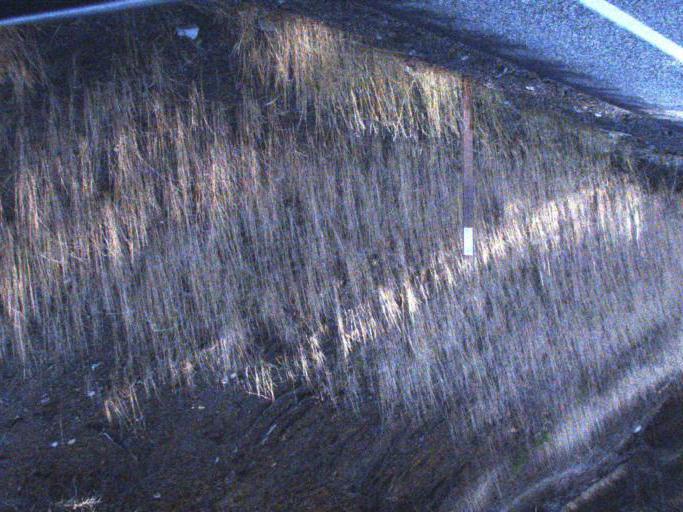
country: US
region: Washington
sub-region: Ferry County
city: Republic
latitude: 48.6110
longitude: -118.5884
